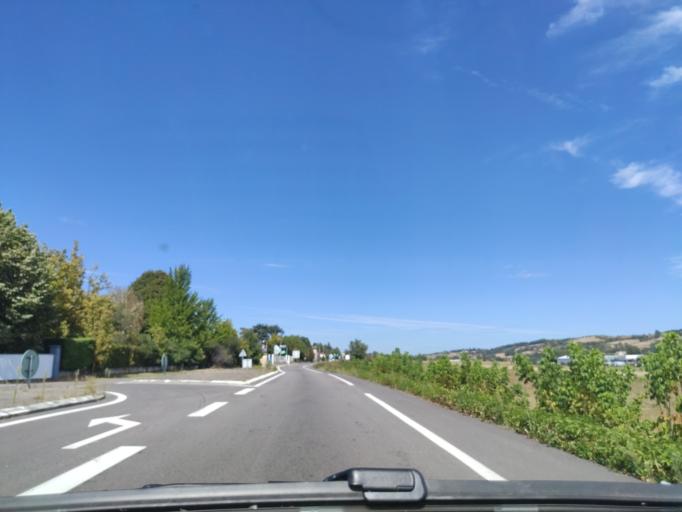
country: FR
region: Rhone-Alpes
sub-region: Departement de l'Isere
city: Reventin-Vaugris
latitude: 45.4600
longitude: 4.8258
